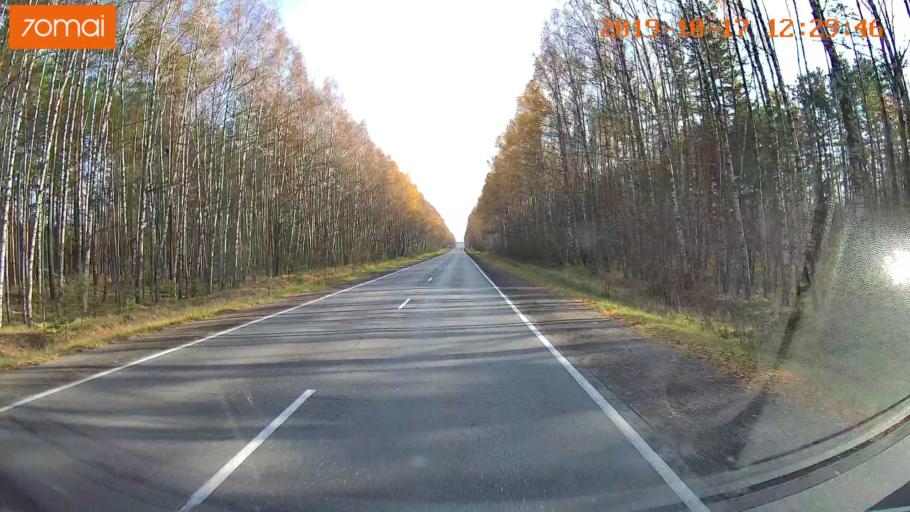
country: RU
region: Rjazan
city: Syntul
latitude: 54.9793
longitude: 41.3001
